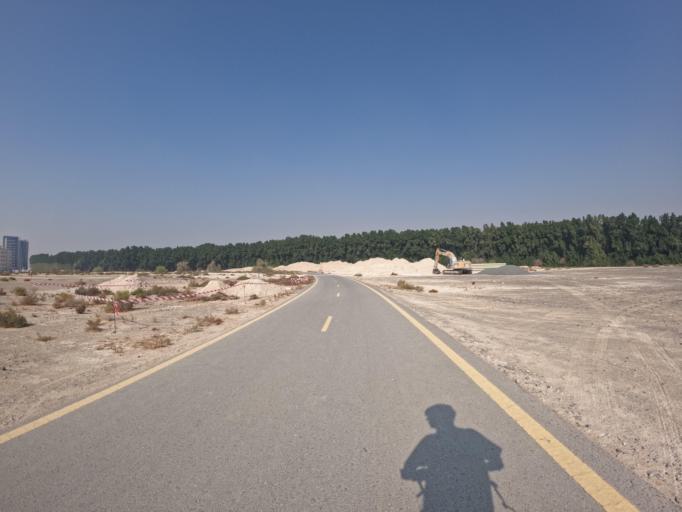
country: AE
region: Dubai
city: Dubai
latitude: 25.0972
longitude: 55.3269
